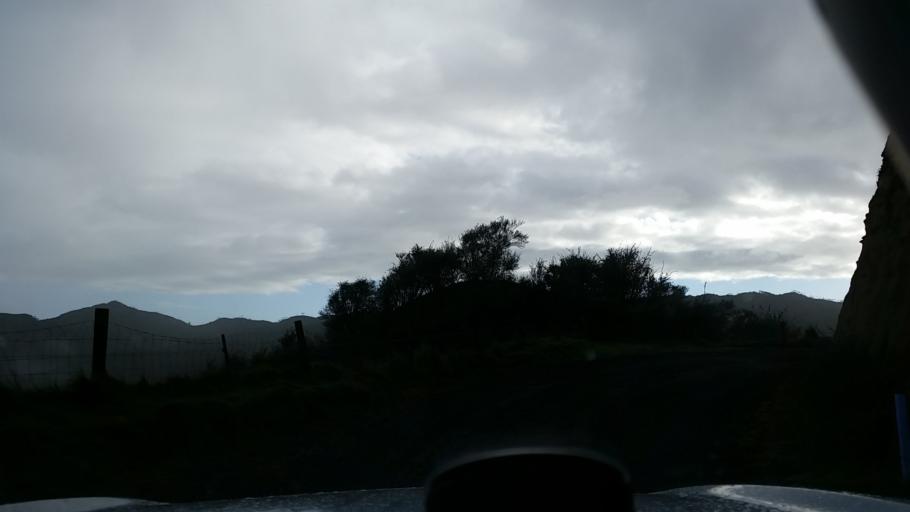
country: NZ
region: Taranaki
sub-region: South Taranaki District
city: Eltham
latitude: -39.4091
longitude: 174.5345
